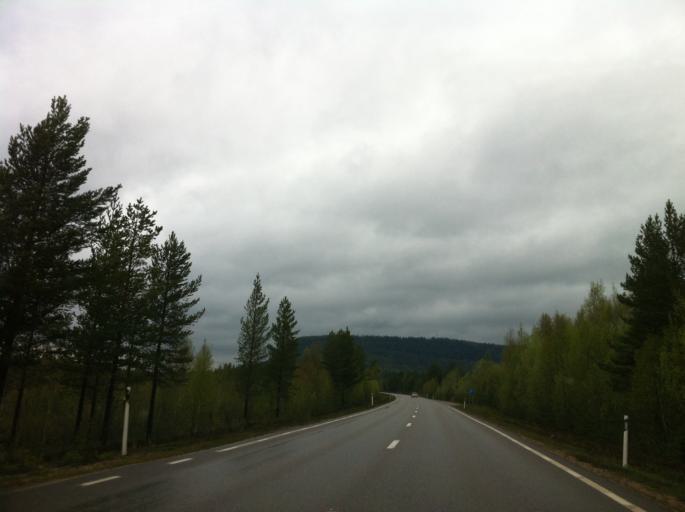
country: SE
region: Jaemtland
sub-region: Harjedalens Kommun
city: Sveg
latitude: 62.0897
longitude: 14.2468
